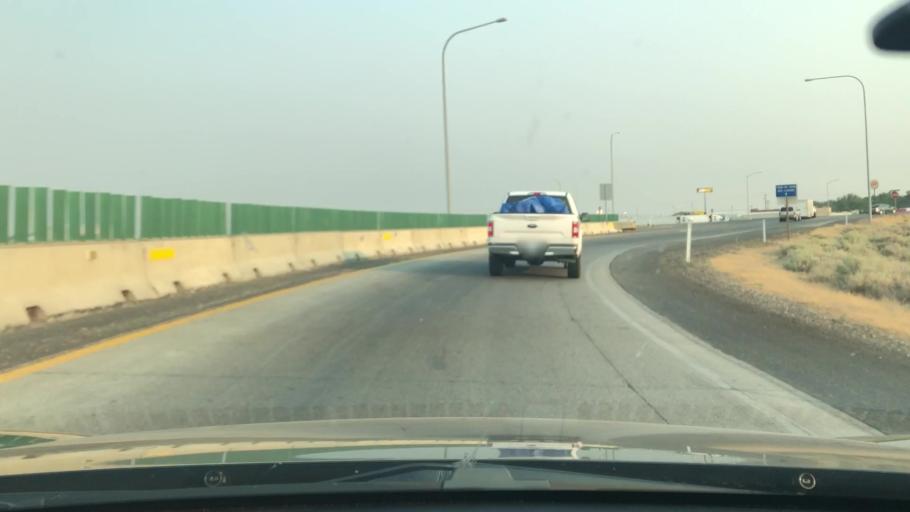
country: US
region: Washington
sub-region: Franklin County
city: Pasco
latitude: 46.2663
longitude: -119.0839
